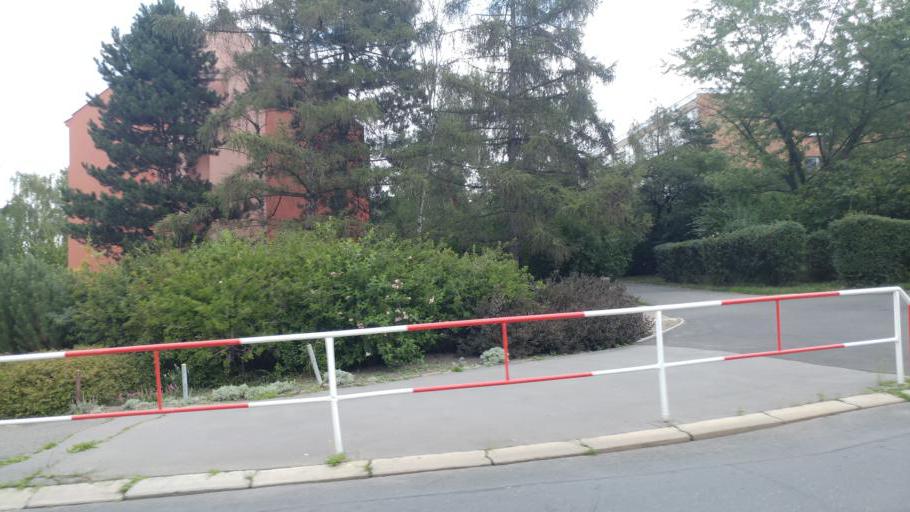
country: CZ
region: Praha
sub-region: Praha 9
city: Vysocany
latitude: 50.0588
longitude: 14.5066
